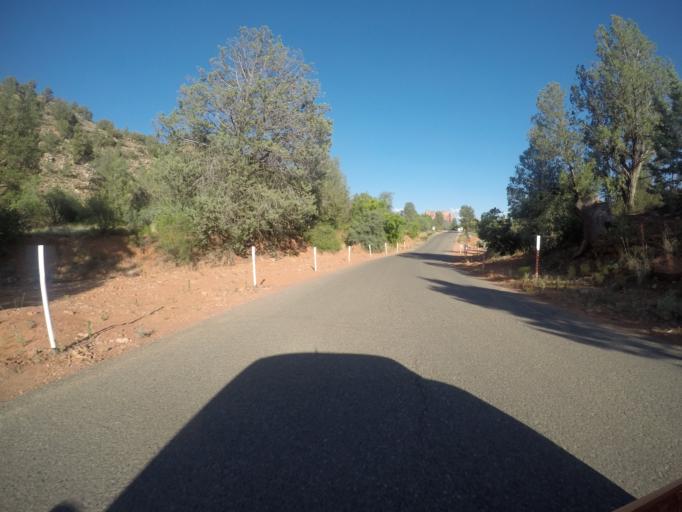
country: US
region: Arizona
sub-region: Yavapai County
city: West Sedona
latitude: 34.8268
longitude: -111.7905
